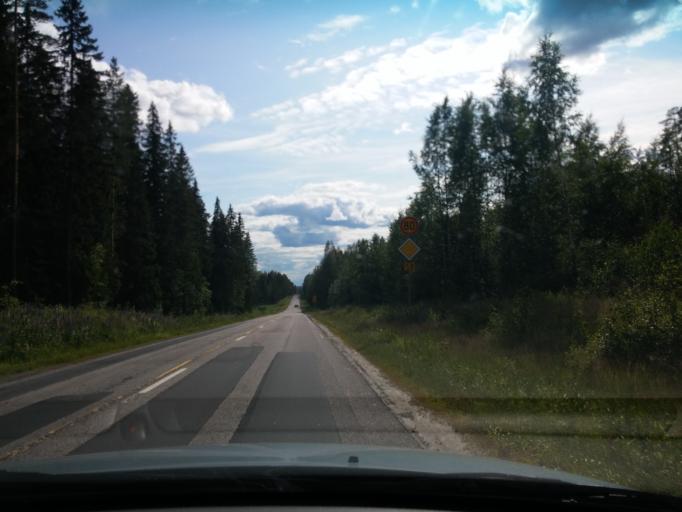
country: FI
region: Central Finland
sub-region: Keuruu
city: Keuruu
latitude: 62.3035
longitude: 24.7230
